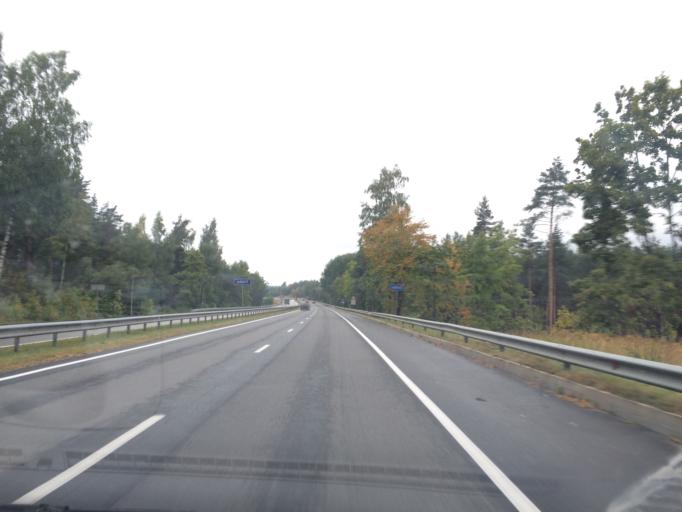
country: LV
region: Ikskile
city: Ikskile
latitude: 56.8417
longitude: 24.4846
